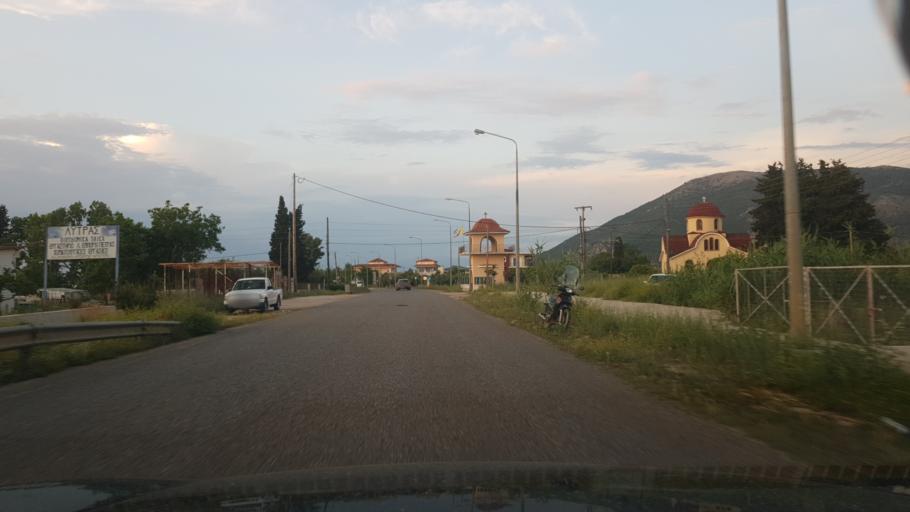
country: GR
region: West Greece
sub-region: Nomos Aitolias kai Akarnanias
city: Vonitsa
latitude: 38.9089
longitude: 20.8859
